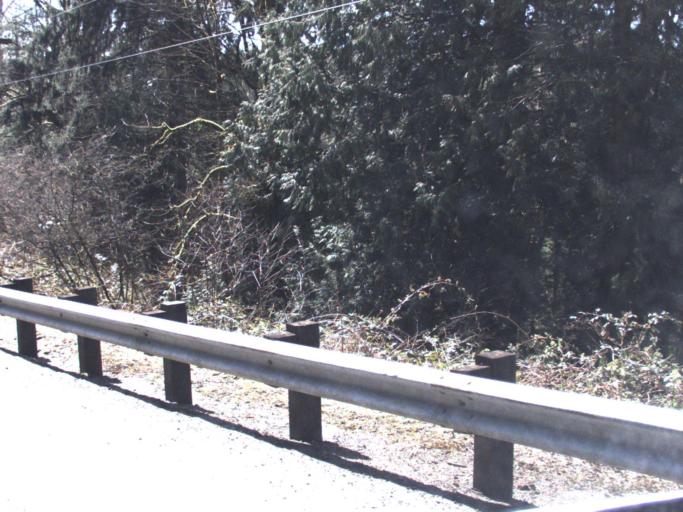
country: US
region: Washington
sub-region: King County
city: Black Diamond
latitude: 47.2794
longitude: -121.9904
